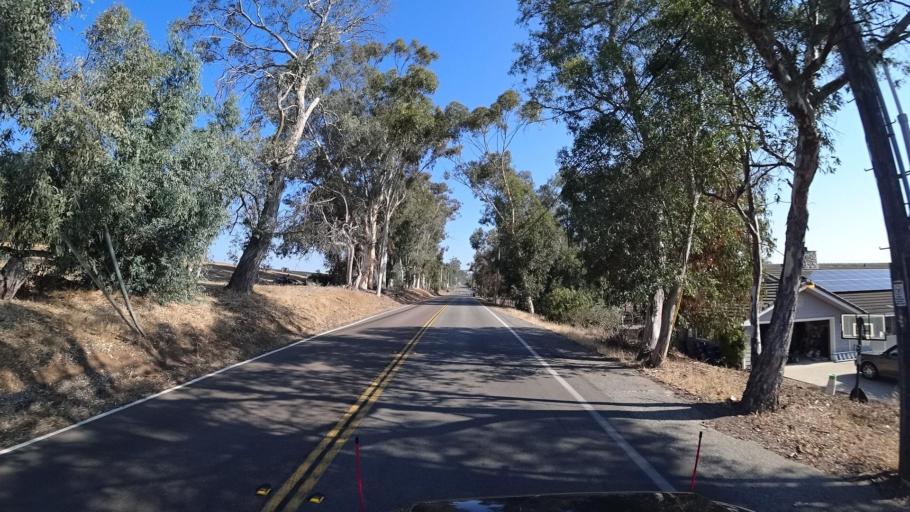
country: US
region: California
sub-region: San Diego County
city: Fallbrook
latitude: 33.3364
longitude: -117.2449
